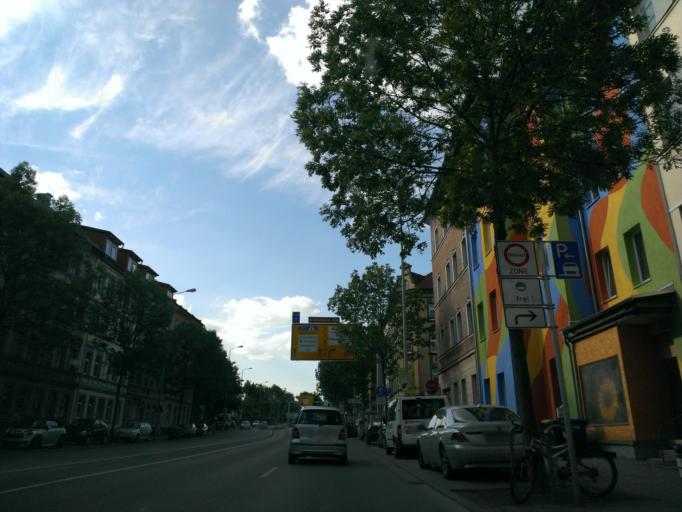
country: DE
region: Thuringia
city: Erfurt
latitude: 50.9728
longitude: 11.0103
